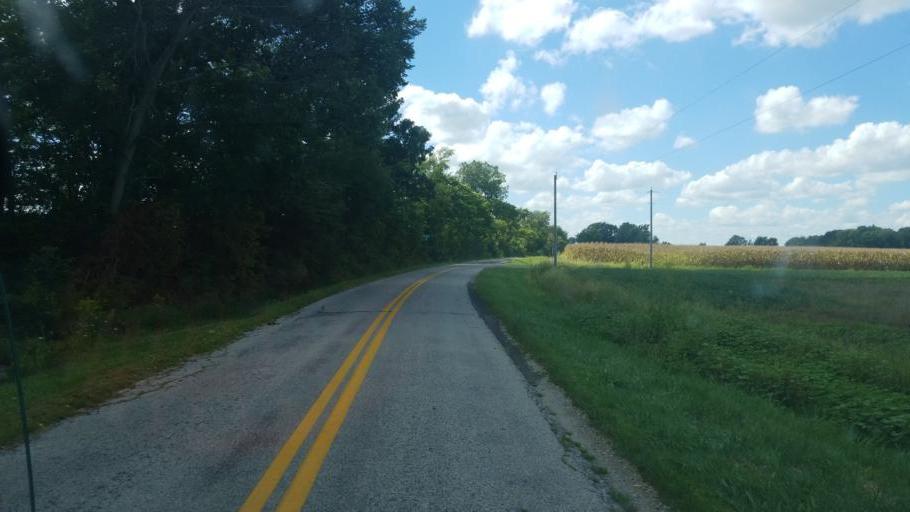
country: US
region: Ohio
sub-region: Union County
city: Richwood
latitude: 40.3506
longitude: -83.2374
